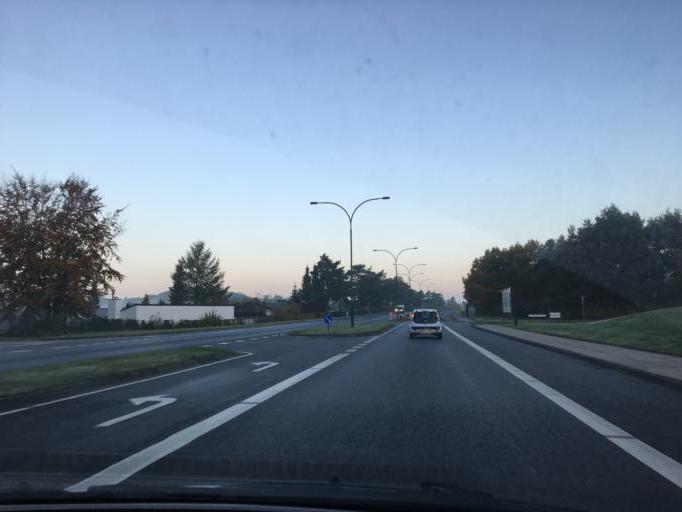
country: DK
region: South Denmark
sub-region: Vejle Kommune
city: Vejle
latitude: 55.6784
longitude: 9.5300
